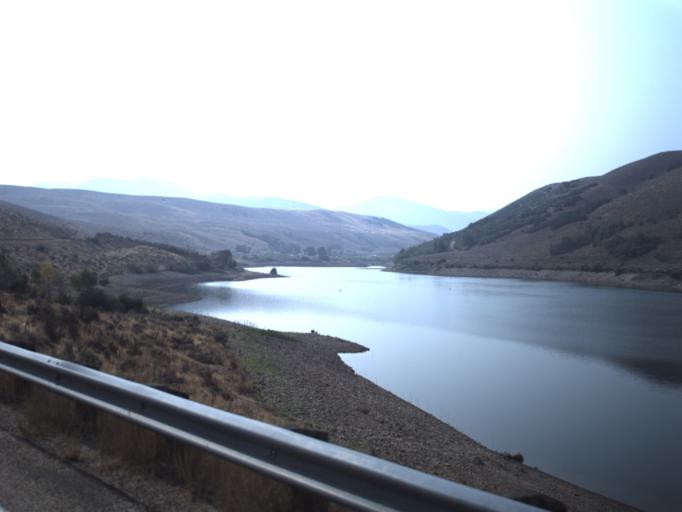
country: US
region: Utah
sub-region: Summit County
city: Summit Park
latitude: 40.8924
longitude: -111.5838
